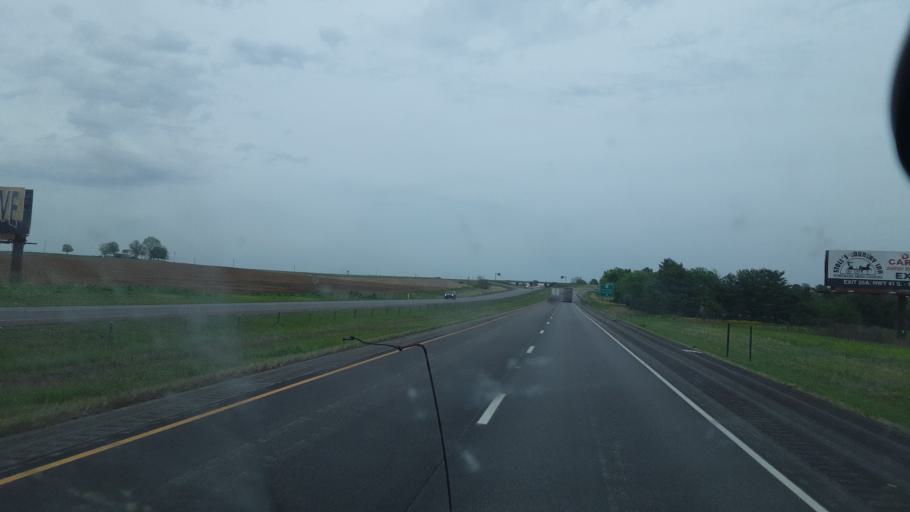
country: US
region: Indiana
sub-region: Posey County
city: Poseyville
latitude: 38.1626
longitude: -87.6944
